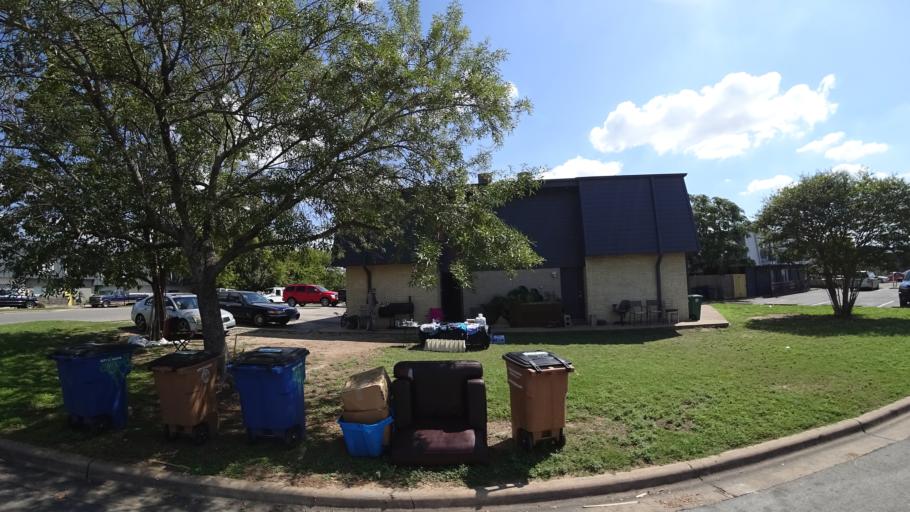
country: US
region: Texas
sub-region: Travis County
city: Austin
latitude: 30.3363
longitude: -97.7077
